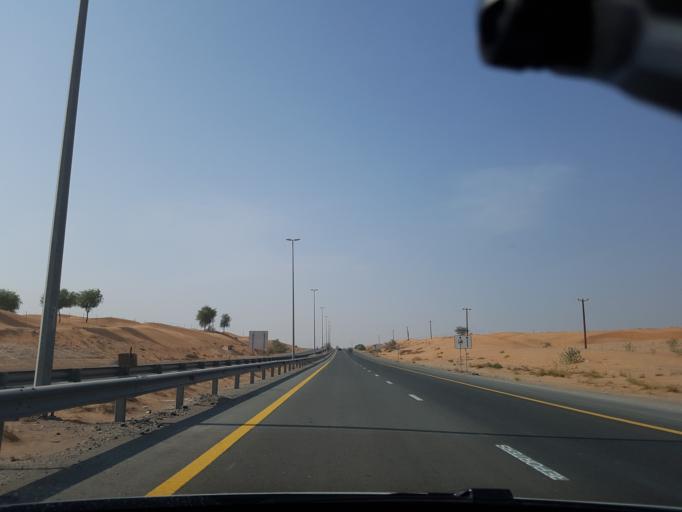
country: AE
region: Umm al Qaywayn
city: Umm al Qaywayn
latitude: 25.5162
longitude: 55.7442
